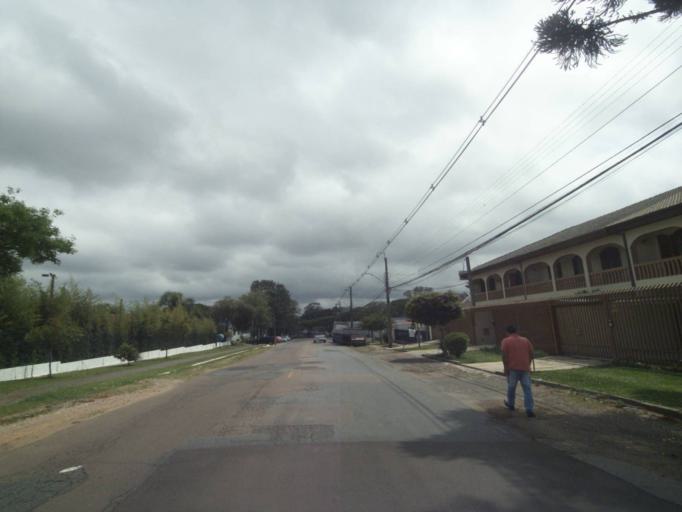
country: BR
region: Parana
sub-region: Pinhais
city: Pinhais
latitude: -25.4302
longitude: -49.2275
